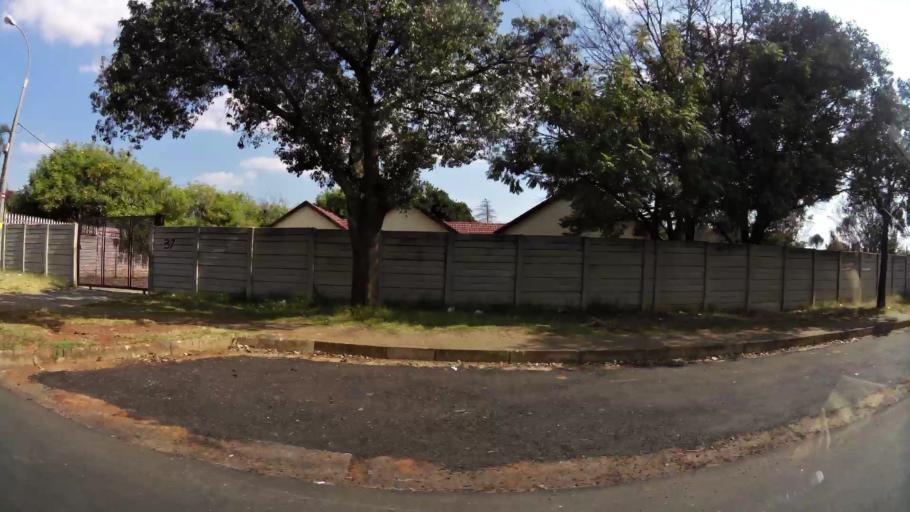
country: ZA
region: Gauteng
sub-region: City of Johannesburg Metropolitan Municipality
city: Modderfontein
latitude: -26.0778
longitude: 28.2379
